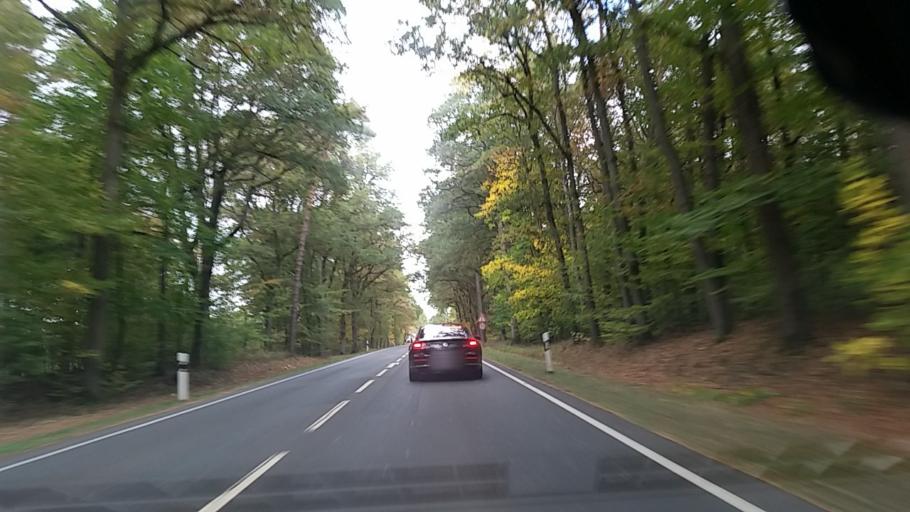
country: DE
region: Lower Saxony
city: Dedelstorf
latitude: 52.7023
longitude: 10.4772
